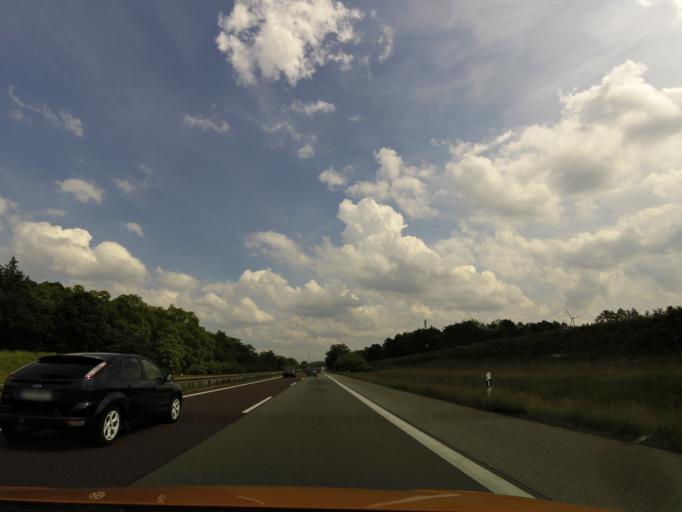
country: DE
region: Brandenburg
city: Triglitz
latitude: 53.2681
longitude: 12.1269
